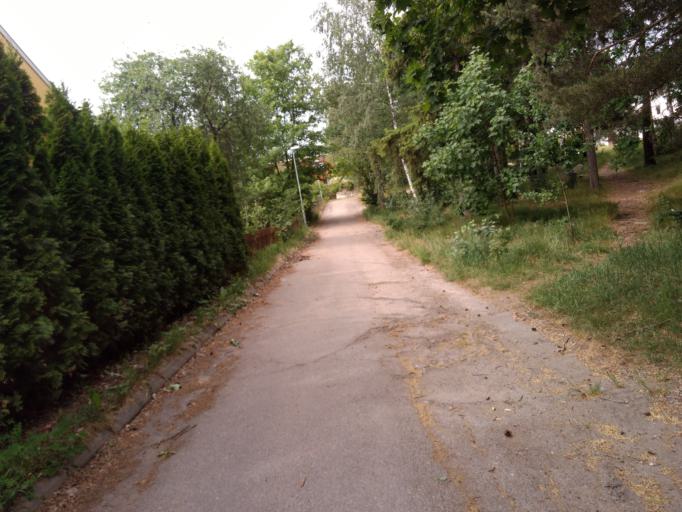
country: SE
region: Stockholm
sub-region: Upplands Vasby Kommun
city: Upplands Vaesby
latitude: 59.5245
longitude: 17.9078
